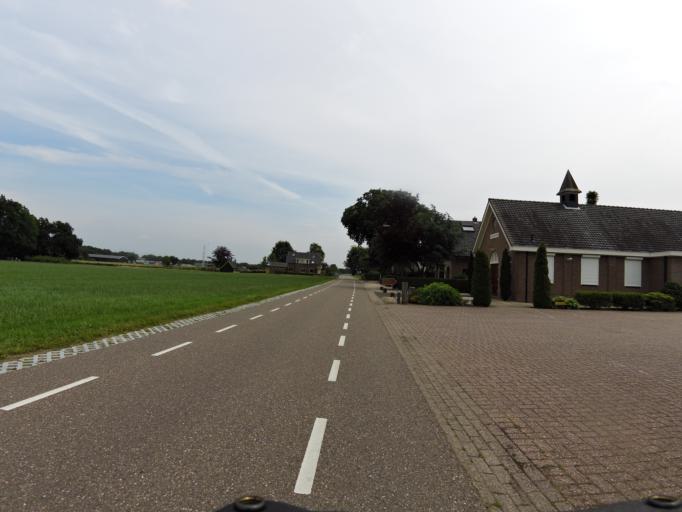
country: NL
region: Gelderland
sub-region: Gemeente Apeldoorn
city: Beekbergen
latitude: 52.1602
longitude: 5.9953
